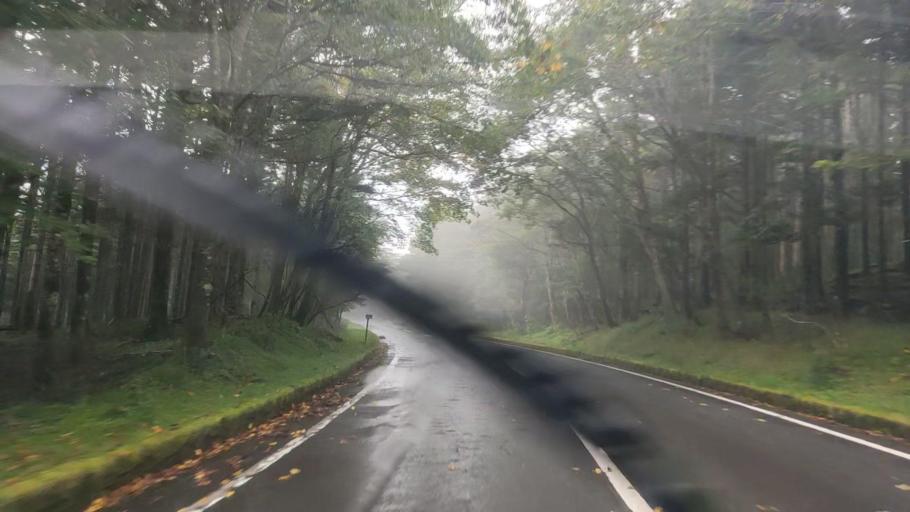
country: JP
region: Shizuoka
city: Fuji
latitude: 35.3052
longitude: 138.7449
